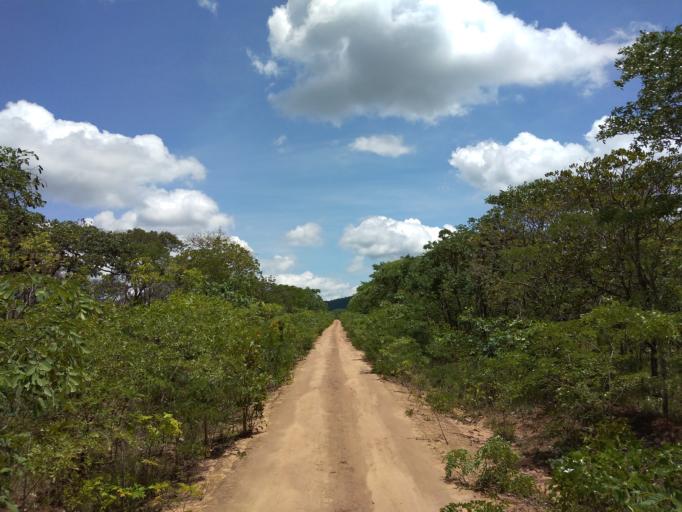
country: ZM
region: Central
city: Mkushi
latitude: -13.9620
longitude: 29.9308
